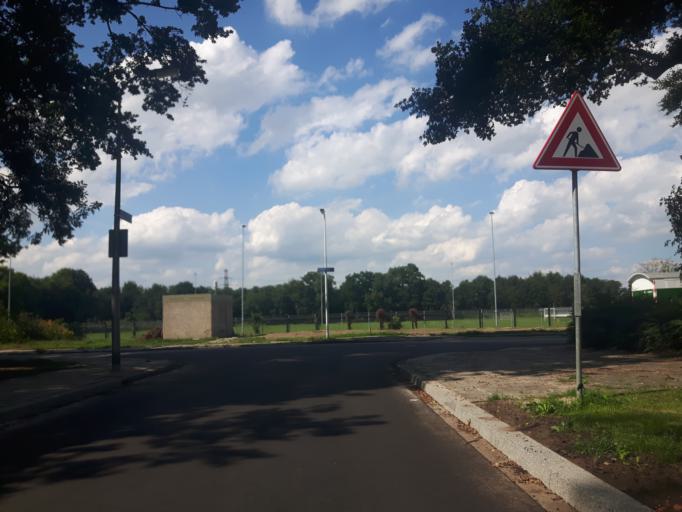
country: NL
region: Overijssel
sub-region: Gemeente Enschede
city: Enschede
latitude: 52.2166
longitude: 6.8555
